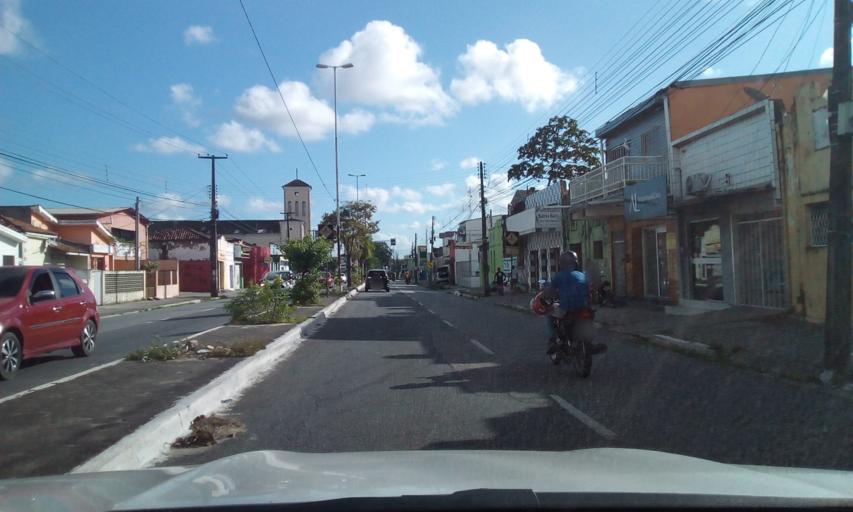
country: BR
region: Paraiba
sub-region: Joao Pessoa
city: Joao Pessoa
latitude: -7.1412
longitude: -34.8897
